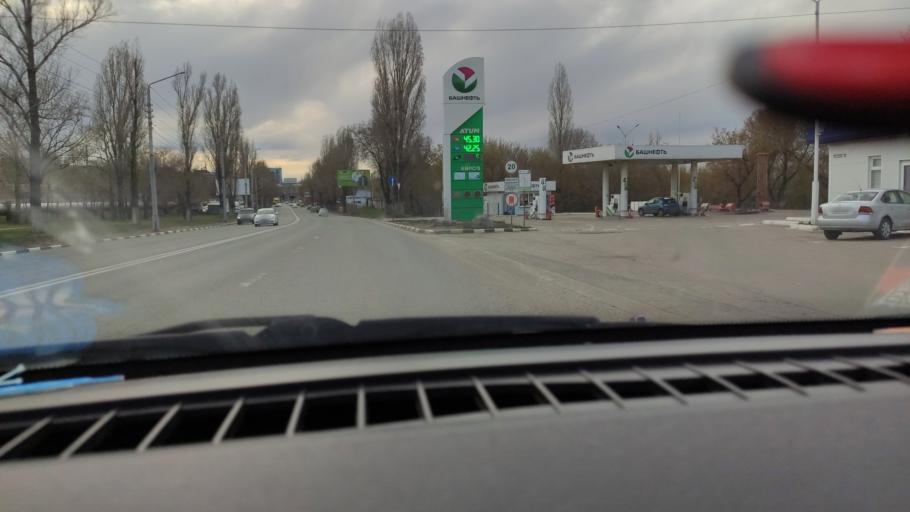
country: RU
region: Saratov
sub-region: Saratovskiy Rayon
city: Saratov
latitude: 51.5808
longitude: 45.9781
